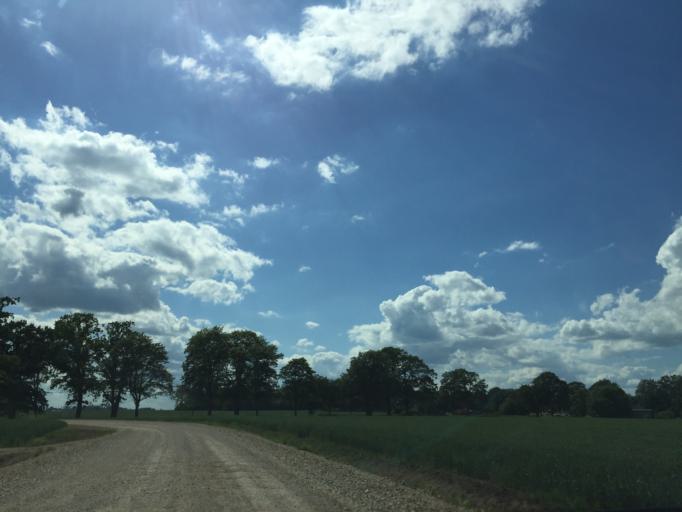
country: LV
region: Engure
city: Smarde
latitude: 56.8673
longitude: 23.3253
